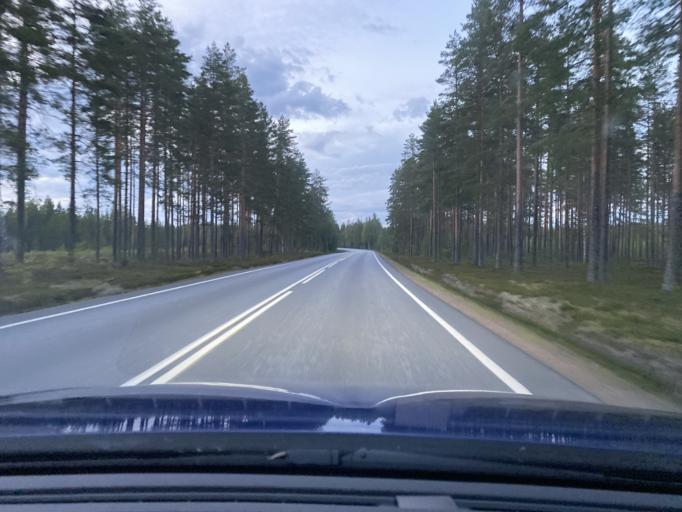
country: FI
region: Southern Ostrobothnia
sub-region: Suupohja
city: Kauhajoki
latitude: 62.2343
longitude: 22.2715
